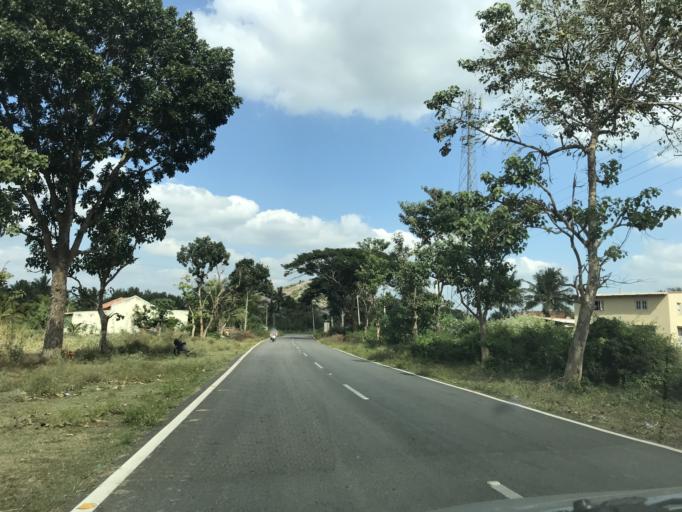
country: IN
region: Karnataka
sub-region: Hassan
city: Shravanabelagola
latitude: 12.8460
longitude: 76.4748
